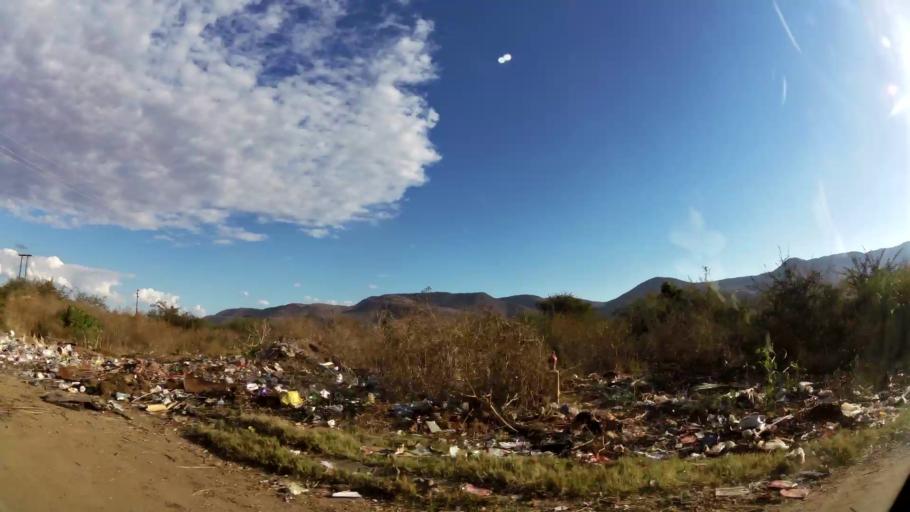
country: ZA
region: Limpopo
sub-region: Waterberg District Municipality
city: Mokopane
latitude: -24.1931
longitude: 28.9810
